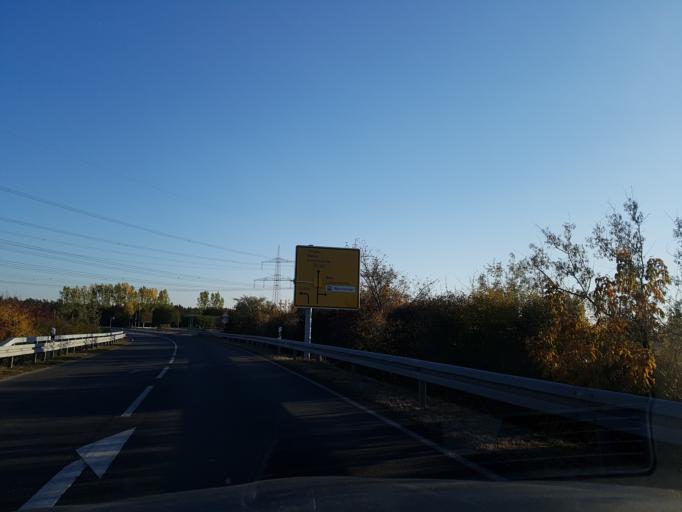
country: DE
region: Brandenburg
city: Bad Liebenwerda
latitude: 51.5156
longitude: 13.4270
